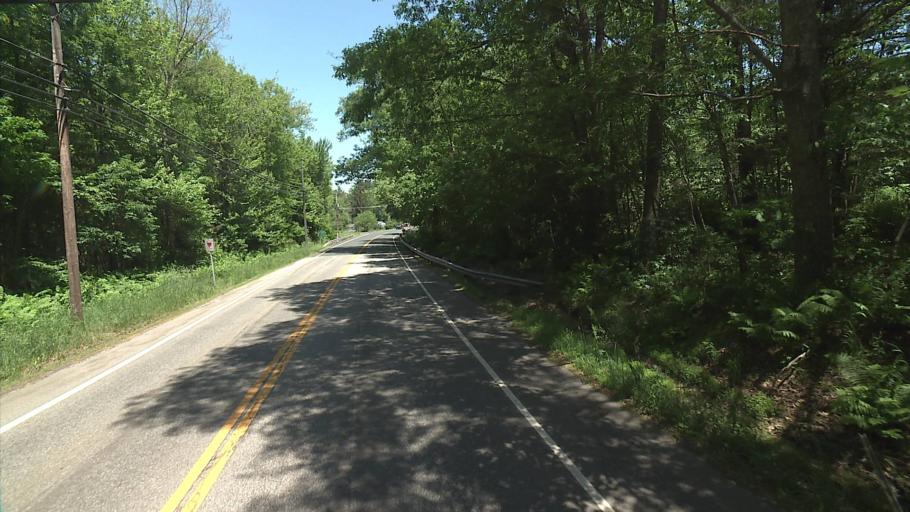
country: US
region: Connecticut
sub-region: Tolland County
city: Crystal Lake
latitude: 41.9193
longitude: -72.3896
